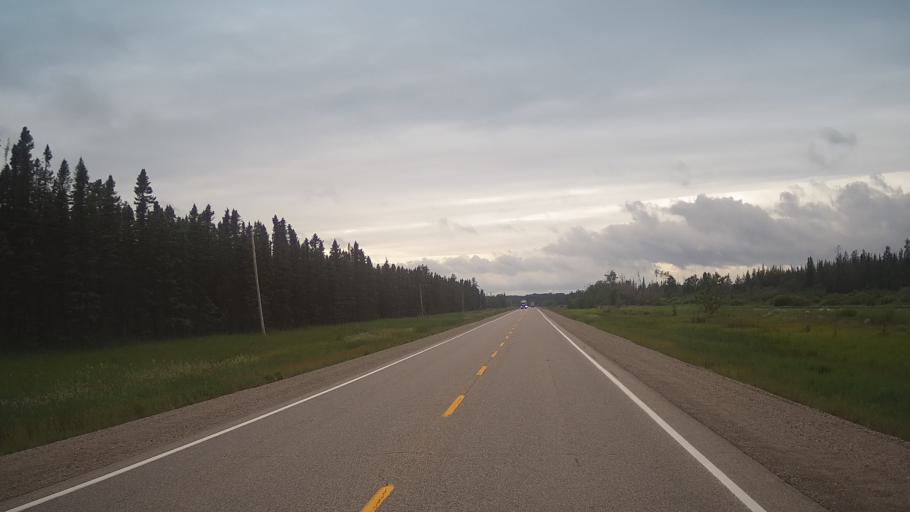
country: CA
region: Ontario
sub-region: Thunder Bay District
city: Thunder Bay
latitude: 48.8944
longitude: -90.0131
